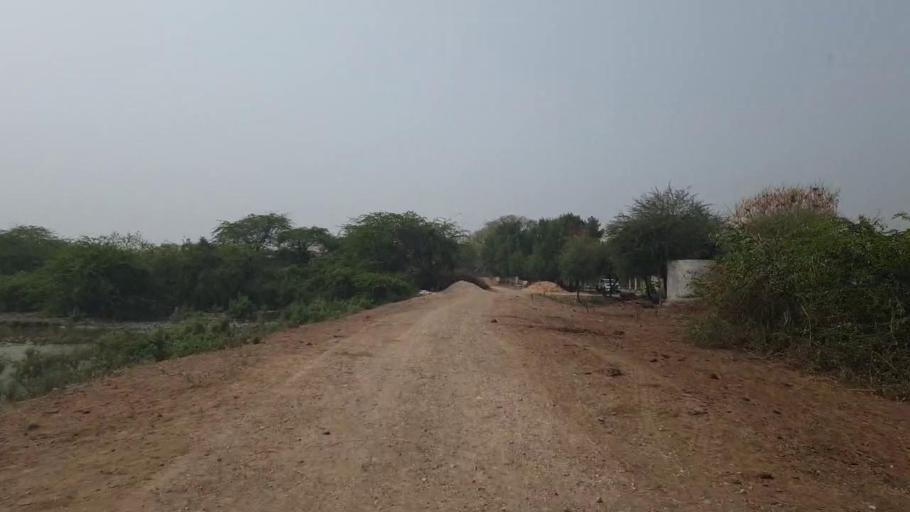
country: PK
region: Sindh
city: Kario
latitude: 24.6527
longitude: 68.6624
